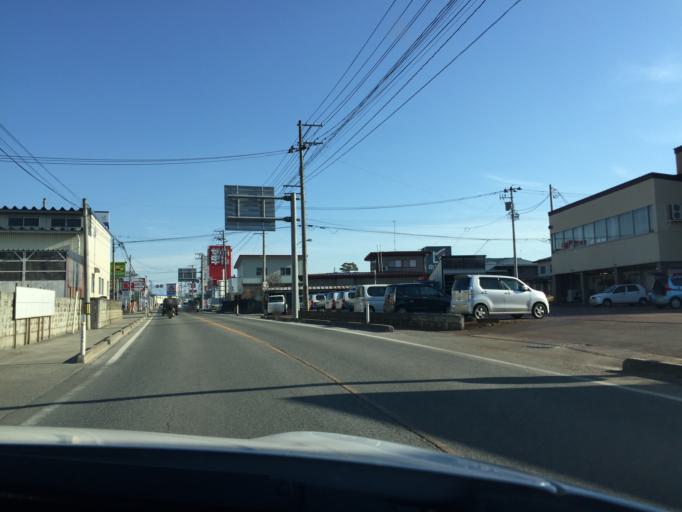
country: JP
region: Yamagata
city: Nagai
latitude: 38.0942
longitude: 140.0415
